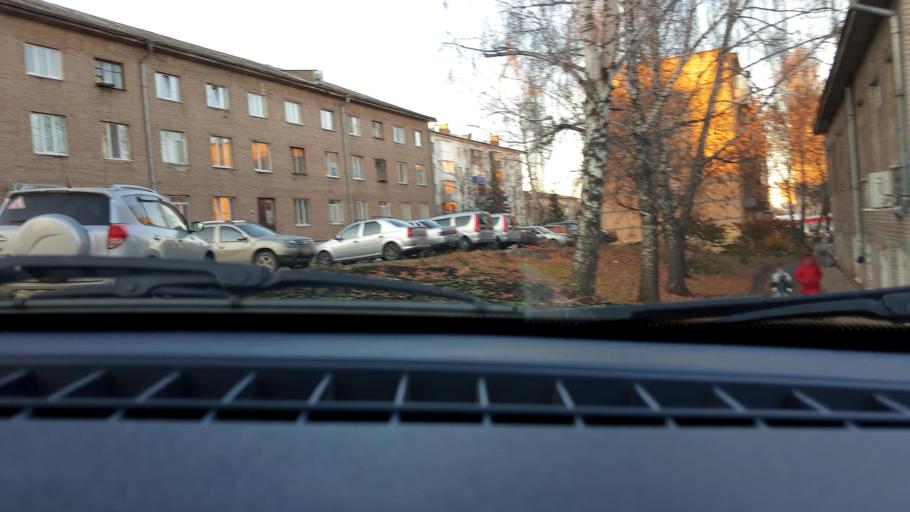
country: RU
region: Bashkortostan
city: Ufa
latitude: 54.7445
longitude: 55.9942
